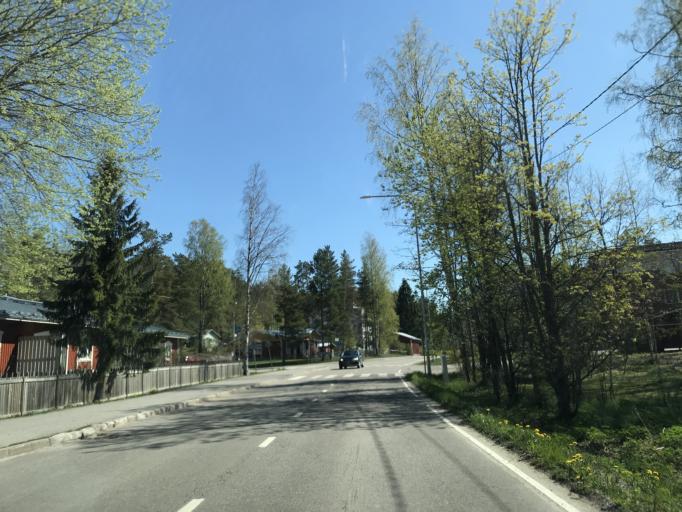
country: FI
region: Paijanne Tavastia
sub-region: Lahti
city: Orimattila
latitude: 60.8151
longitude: 25.7335
